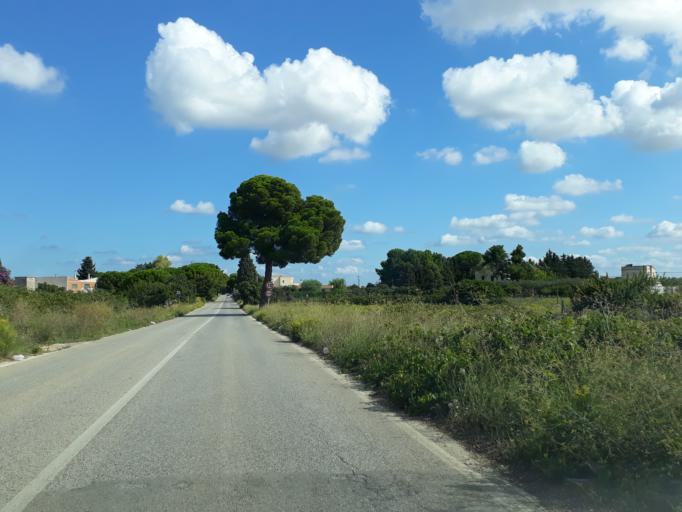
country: IT
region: Apulia
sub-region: Provincia di Bari
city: Rutigliano
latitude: 41.0155
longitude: 17.0168
